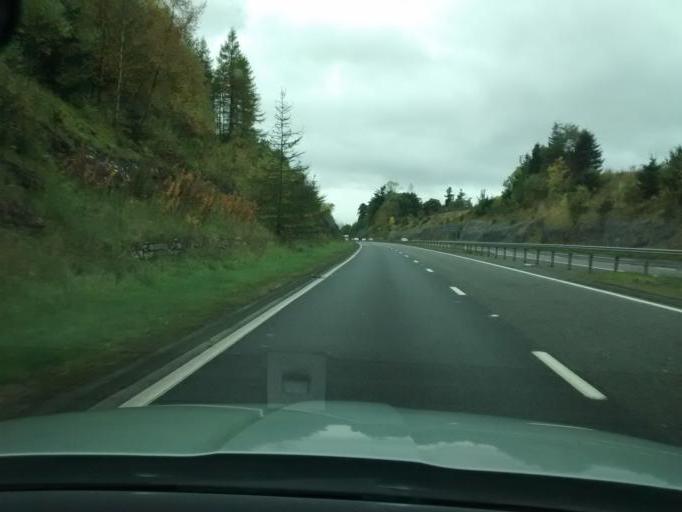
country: GB
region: Scotland
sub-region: Perth and Kinross
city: Methven
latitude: 56.3717
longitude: -3.5430
